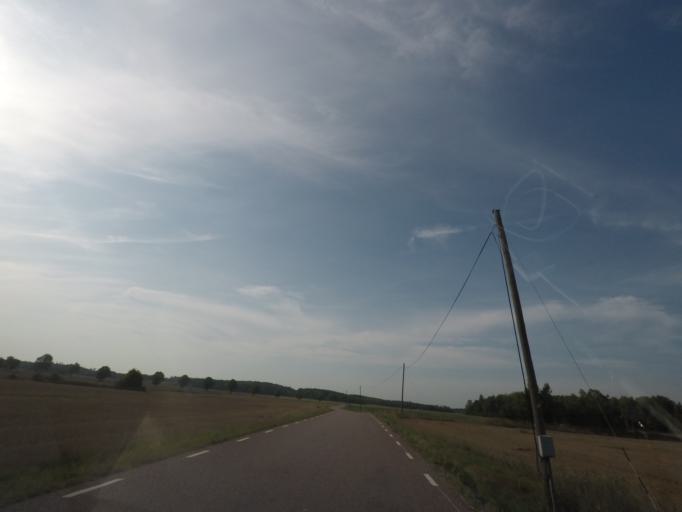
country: SE
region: Vaestmanland
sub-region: Hallstahammars Kommun
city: Kolback
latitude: 59.5248
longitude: 16.1863
